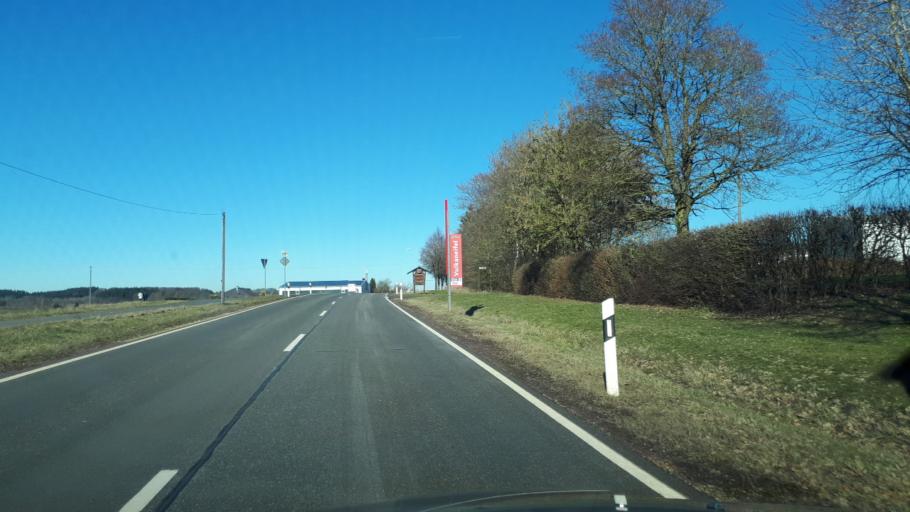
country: DE
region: Rheinland-Pfalz
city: Strotzbusch
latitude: 50.1049
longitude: 6.9651
